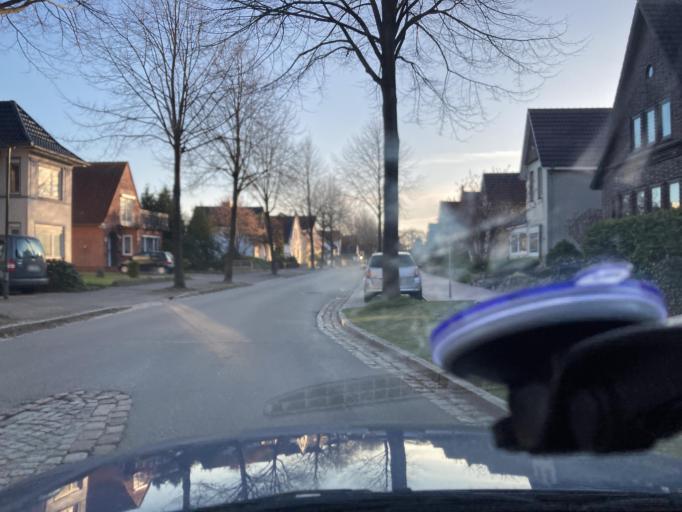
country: DE
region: Schleswig-Holstein
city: Wesseln
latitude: 54.1918
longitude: 9.0819
